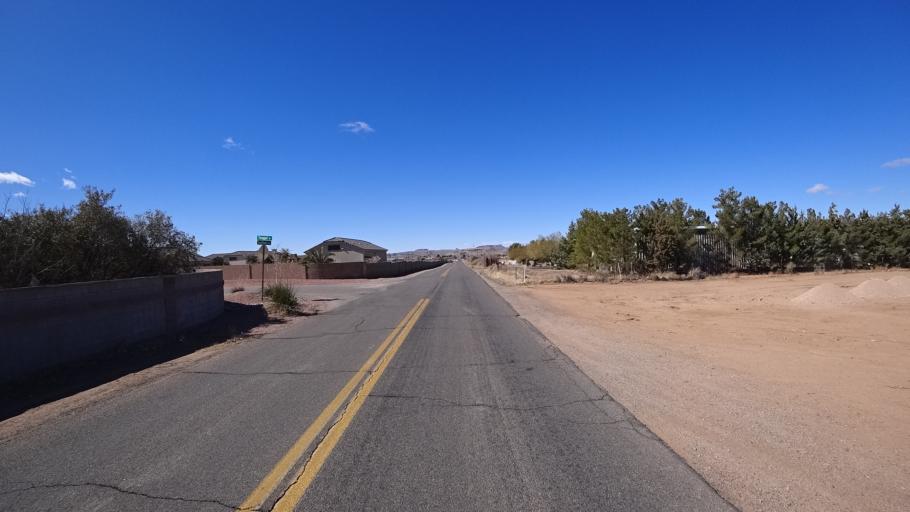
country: US
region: Arizona
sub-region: Mohave County
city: Kingman
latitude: 35.1958
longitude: -113.9980
